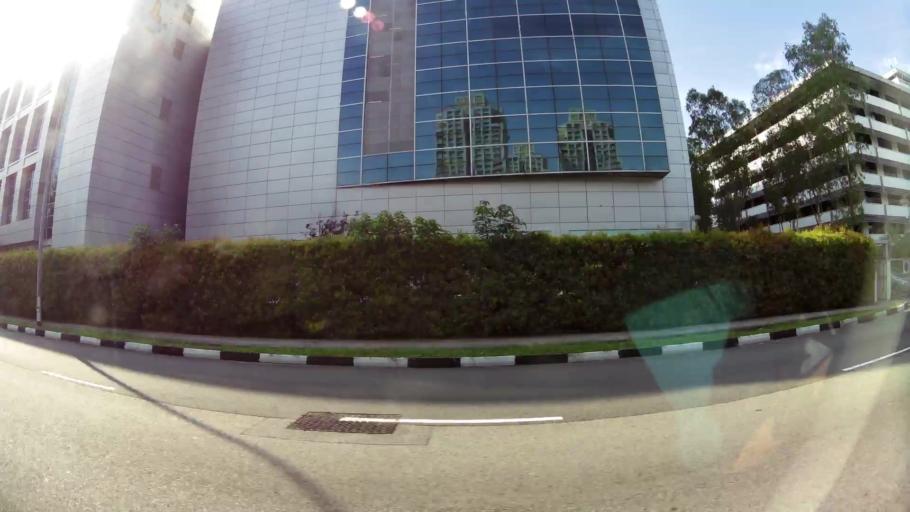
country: SG
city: Singapore
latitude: 1.3437
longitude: 103.8480
